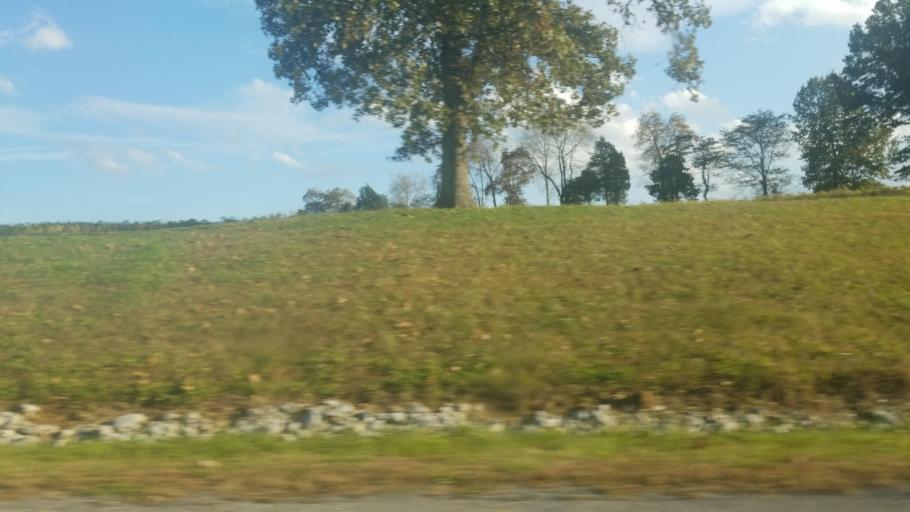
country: US
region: Illinois
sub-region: Williamson County
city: Johnston City
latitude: 37.7663
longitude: -88.7752
